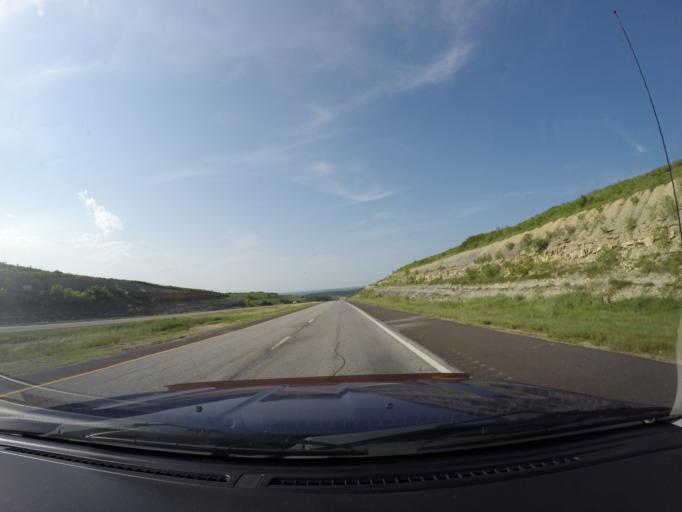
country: US
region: Kansas
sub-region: Riley County
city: Manhattan
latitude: 39.1397
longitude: -96.5380
